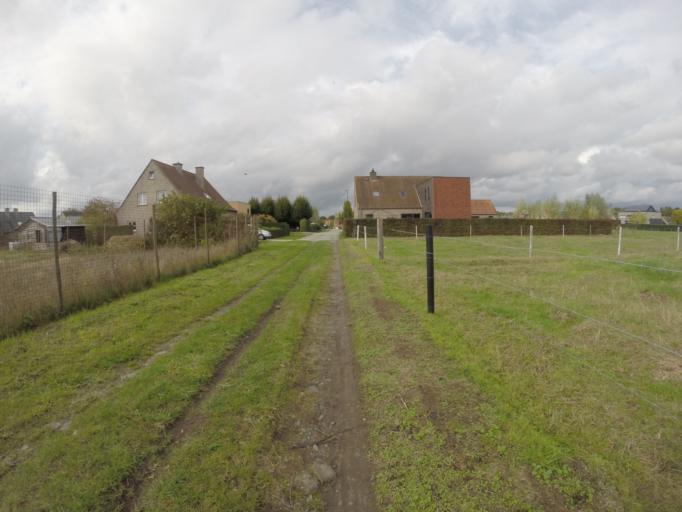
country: BE
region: Flanders
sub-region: Provincie West-Vlaanderen
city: Beernem
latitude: 51.0936
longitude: 3.3727
